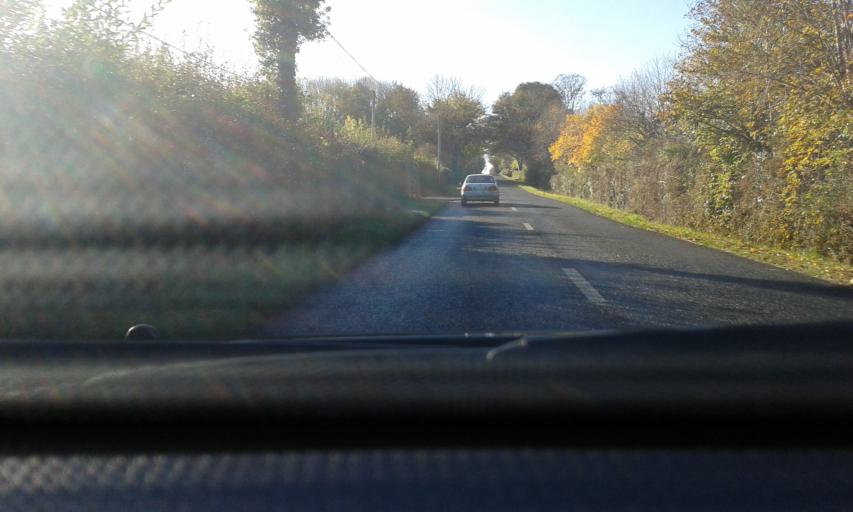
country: IE
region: Leinster
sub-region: Kildare
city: Rathangan
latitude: 53.1932
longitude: -7.0093
